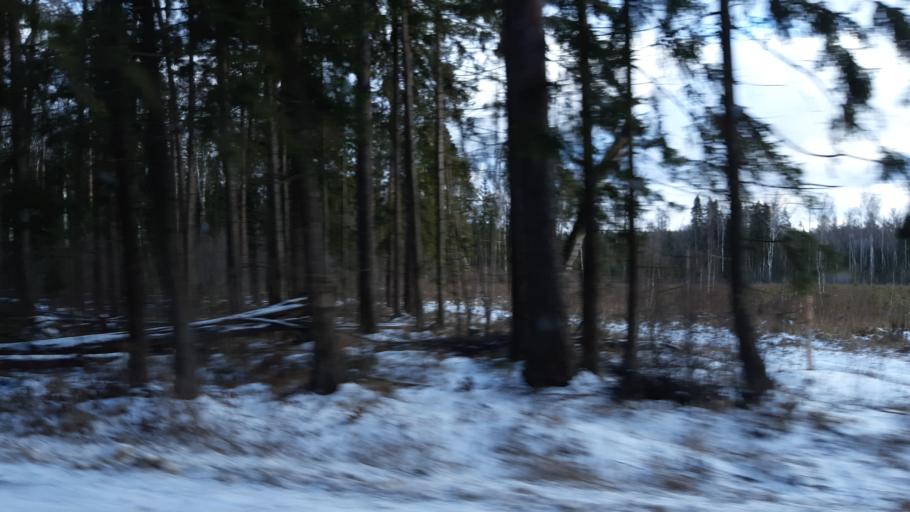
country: RU
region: Moskovskaya
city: Noginsk-9
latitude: 55.9699
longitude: 38.5371
